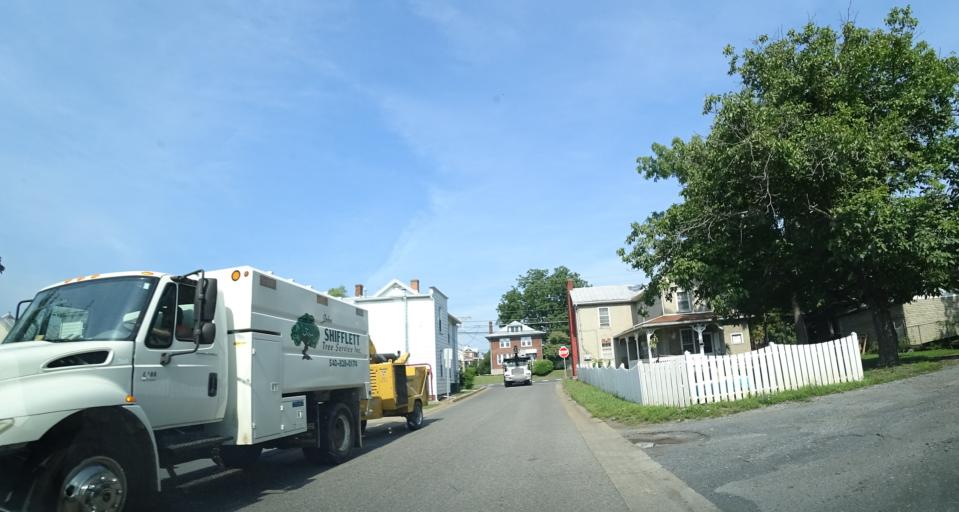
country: US
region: Virginia
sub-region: City of Harrisonburg
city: Harrisonburg
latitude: 38.4530
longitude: -78.8712
